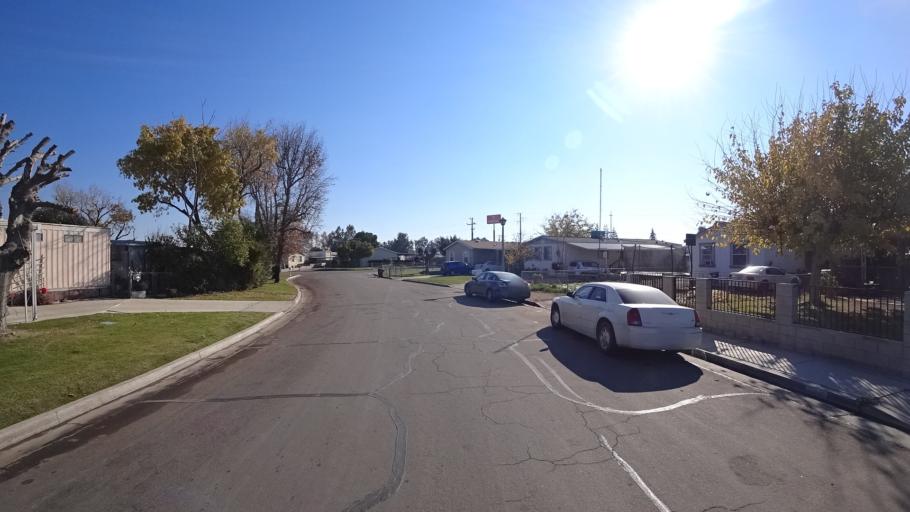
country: US
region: California
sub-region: Kern County
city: Greenfield
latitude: 35.2973
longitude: -119.0337
